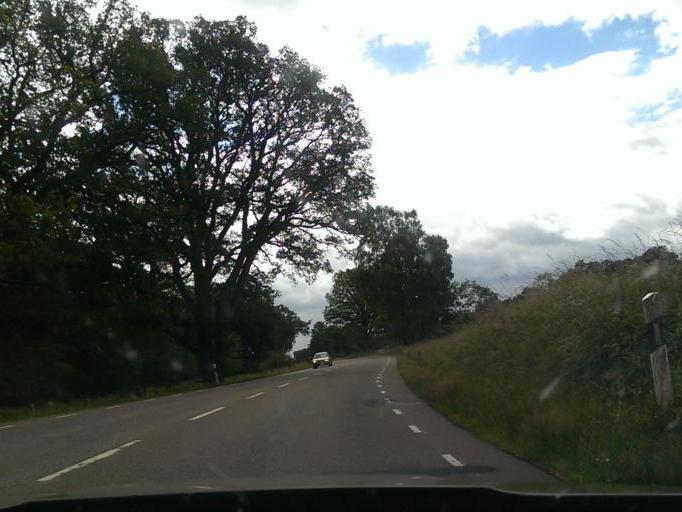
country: SE
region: Skane
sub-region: Klippans Kommun
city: Ljungbyhed
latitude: 56.0079
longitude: 13.2845
